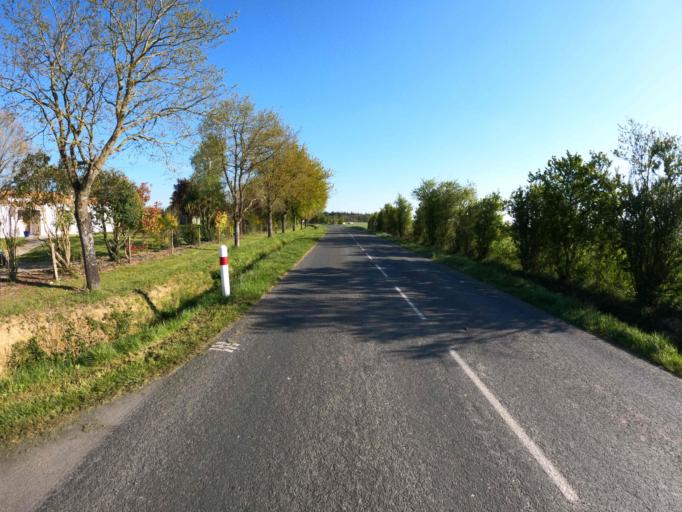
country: FR
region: Pays de la Loire
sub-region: Departement de la Vendee
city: Les Brouzils
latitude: 46.8761
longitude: -1.3256
